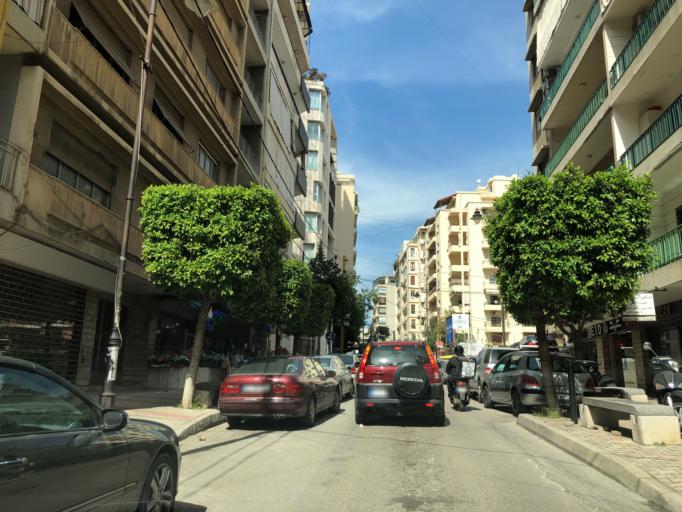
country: LB
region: Beyrouth
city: Beirut
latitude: 33.8853
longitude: 35.5190
